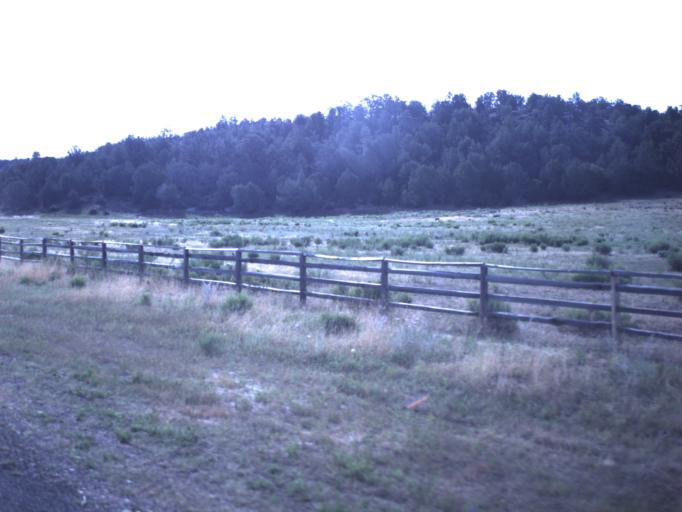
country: US
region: Utah
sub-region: Washington County
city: Hildale
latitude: 37.2395
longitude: -112.8305
